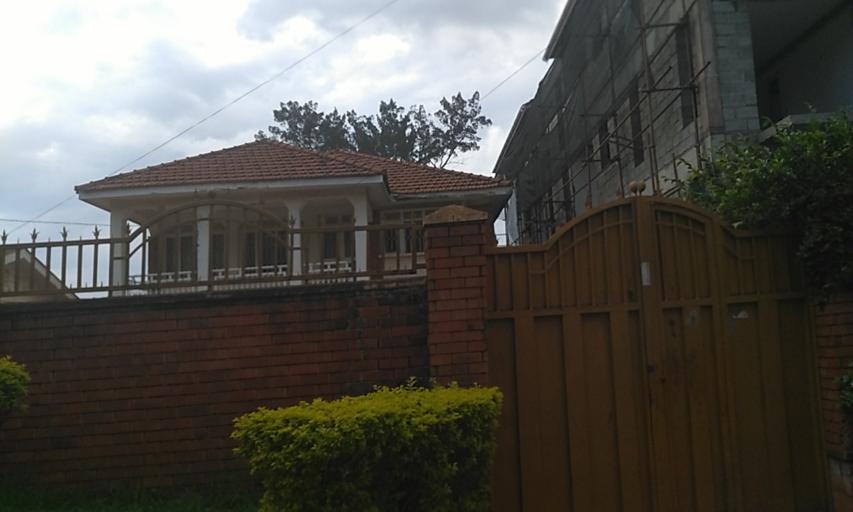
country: UG
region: Central Region
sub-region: Wakiso District
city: Kireka
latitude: 0.3444
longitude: 32.6177
